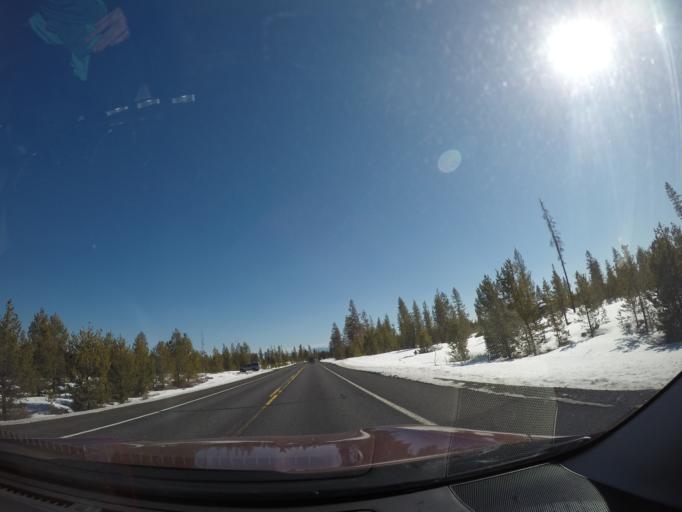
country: US
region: Oregon
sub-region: Deschutes County
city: Three Rivers
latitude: 43.8699
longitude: -121.5476
